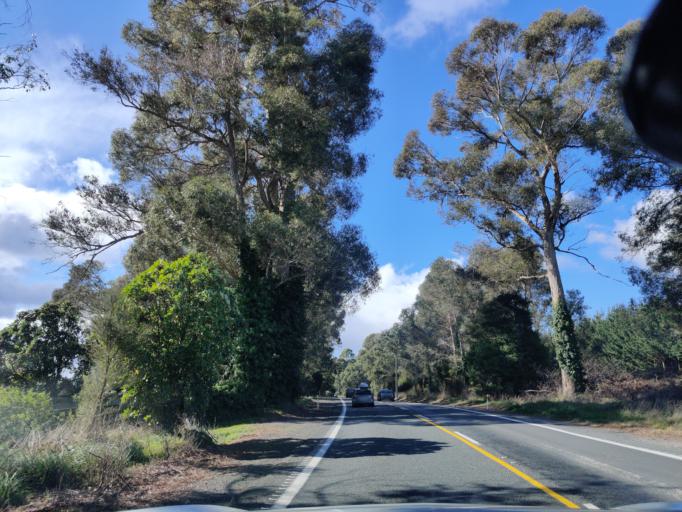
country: NZ
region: Waikato
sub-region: Taupo District
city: Taupo
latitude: -38.8719
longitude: 176.0047
